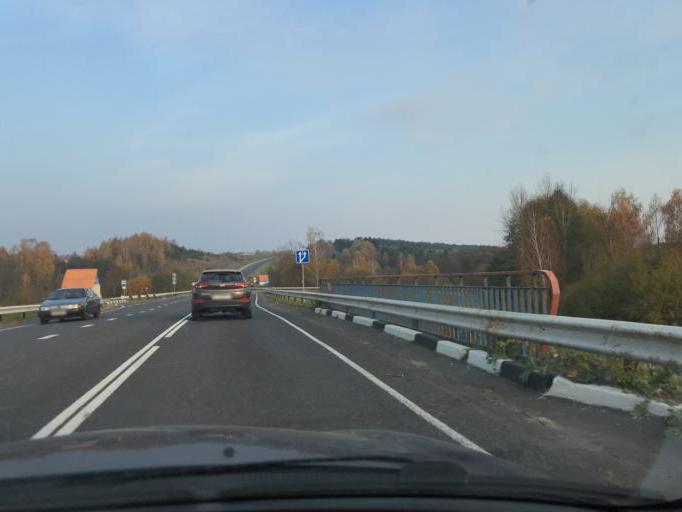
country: BY
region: Grodnenskaya
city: Karelichy
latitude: 53.5963
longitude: 26.0478
